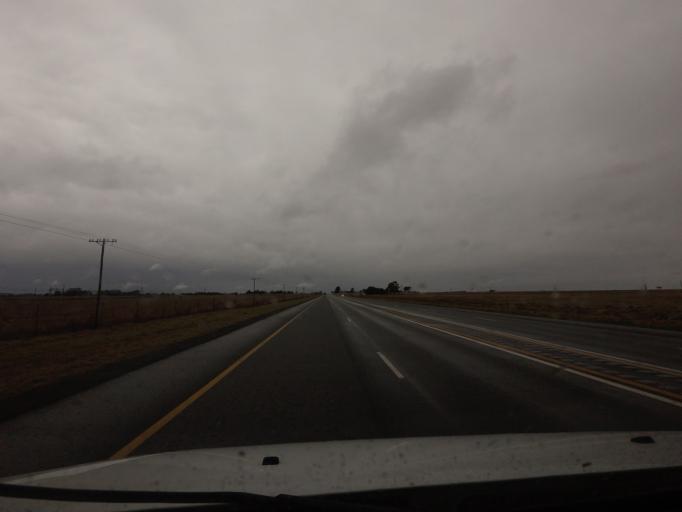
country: ZA
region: Mpumalanga
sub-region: Nkangala District Municipality
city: Belfast
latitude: -25.7242
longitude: 30.0372
